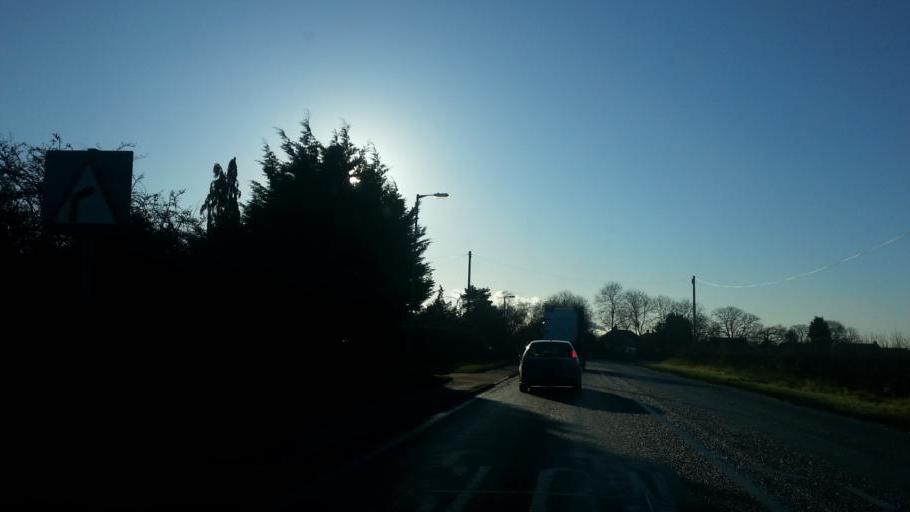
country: GB
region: England
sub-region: Nottinghamshire
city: Newark on Trent
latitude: 53.1096
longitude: -0.8200
